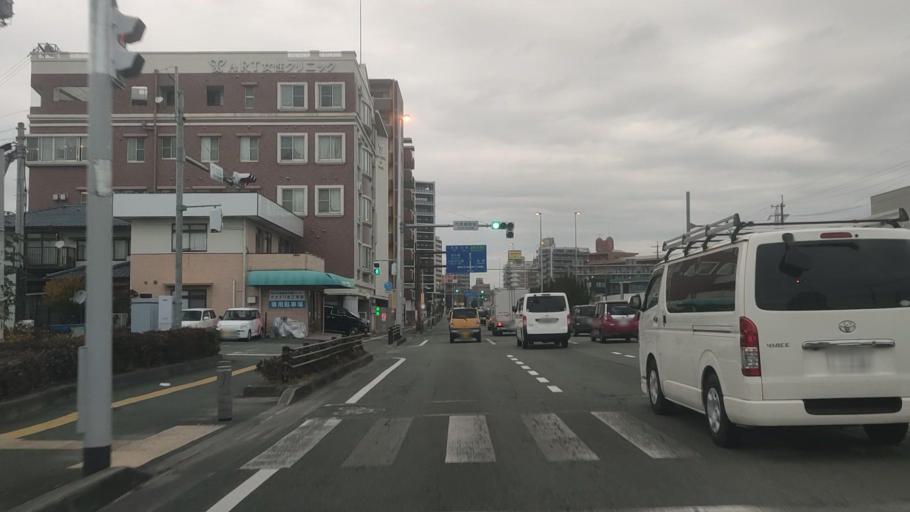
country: JP
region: Kumamoto
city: Kumamoto
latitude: 32.7807
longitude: 130.7444
